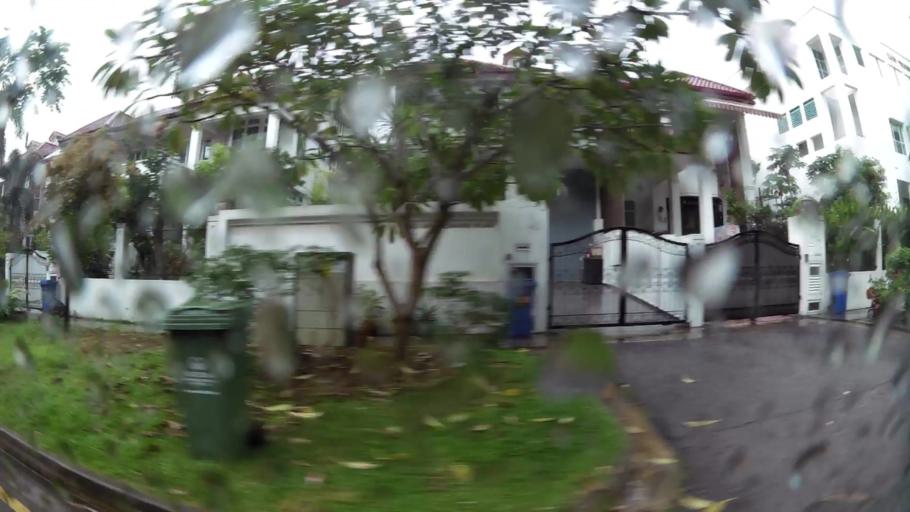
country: SG
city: Singapore
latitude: 1.3357
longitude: 103.9539
